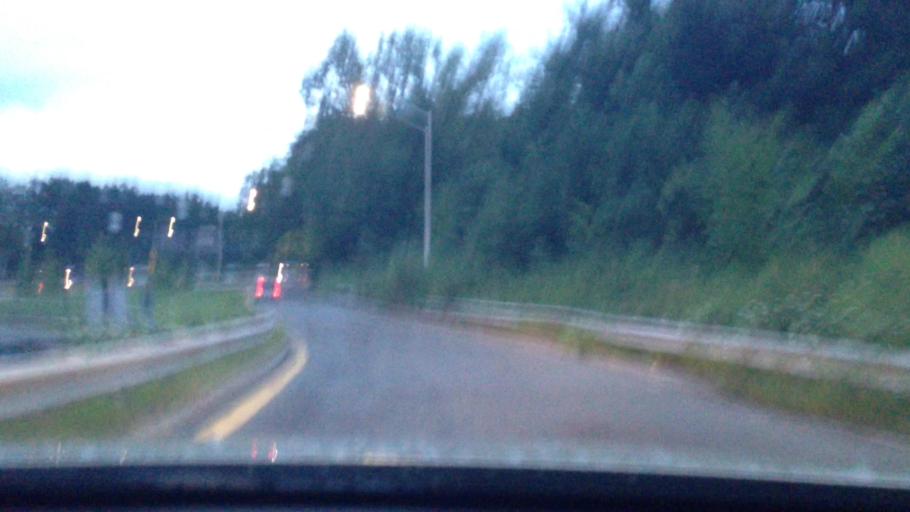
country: US
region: New York
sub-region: Nassau County
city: East Atlantic Beach
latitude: 40.7609
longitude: -73.7568
